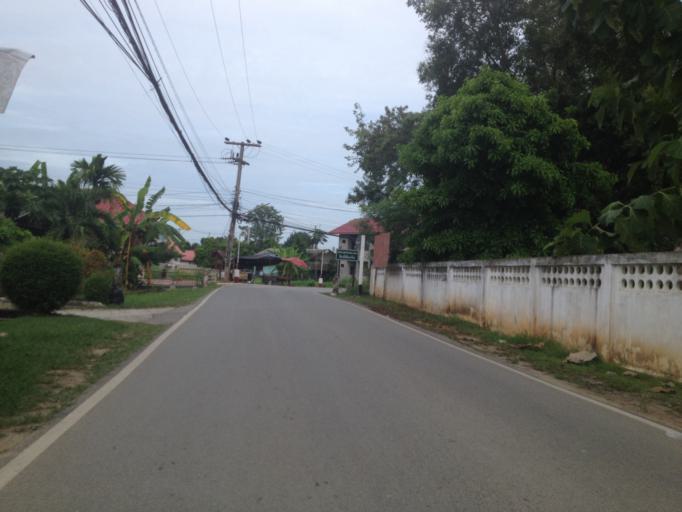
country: TH
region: Chiang Mai
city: Hang Dong
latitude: 18.6962
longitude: 98.9163
